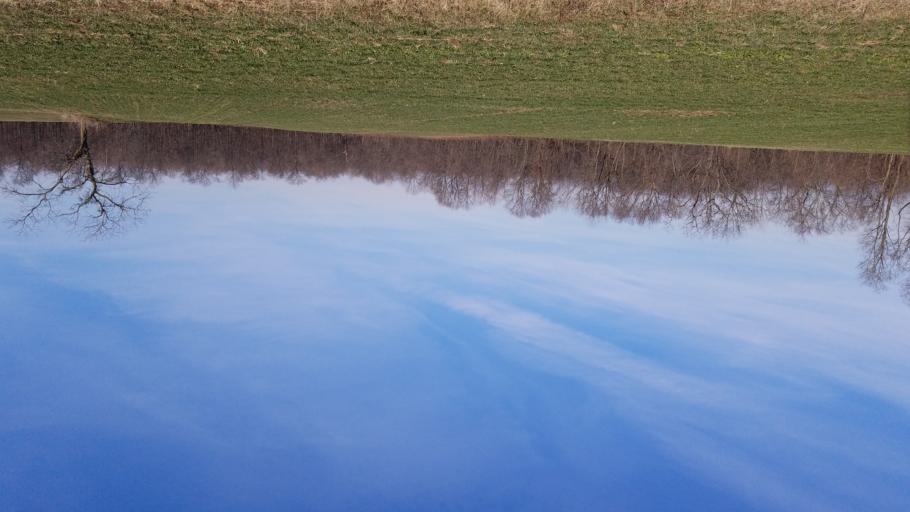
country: US
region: Ohio
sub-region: Knox County
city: Fredericktown
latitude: 40.4910
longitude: -82.6275
